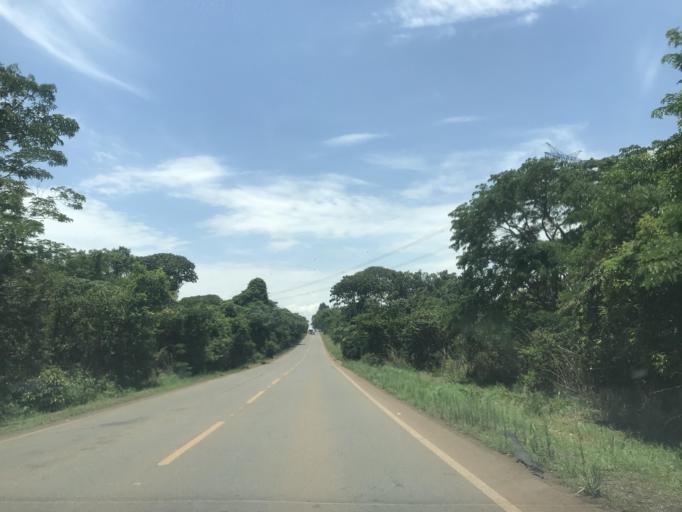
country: BR
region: Goias
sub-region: Vianopolis
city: Vianopolis
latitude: -16.6261
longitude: -48.3544
